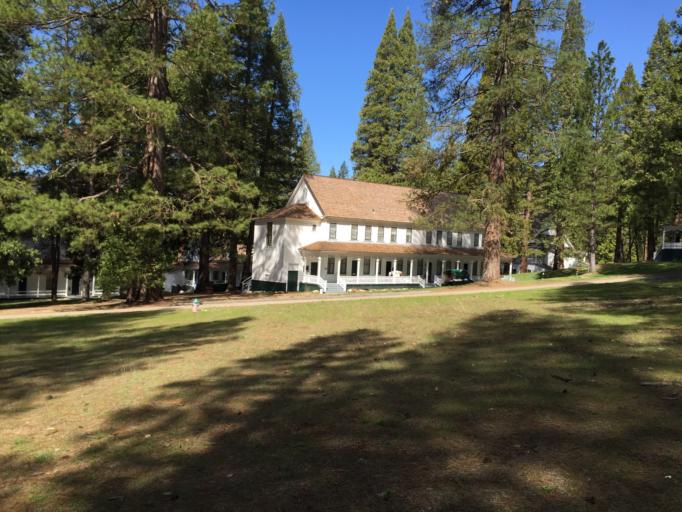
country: US
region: California
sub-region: Madera County
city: Ahwahnee
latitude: 37.5360
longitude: -119.6539
